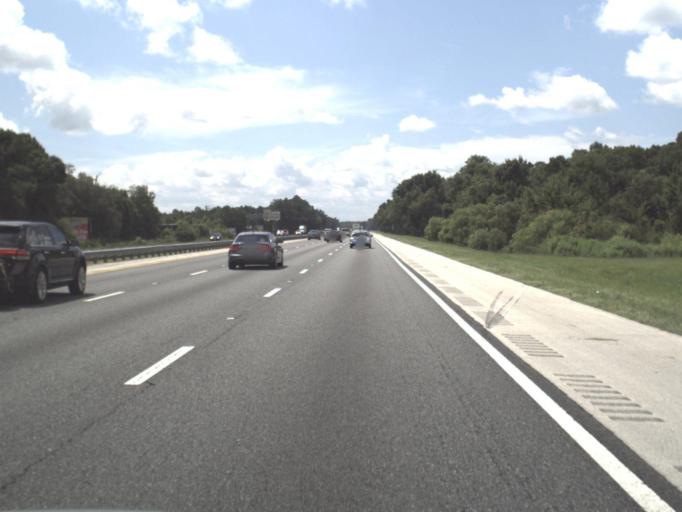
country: US
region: Florida
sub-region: Saint Johns County
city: Villano Beach
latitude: 29.9718
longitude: -81.4533
